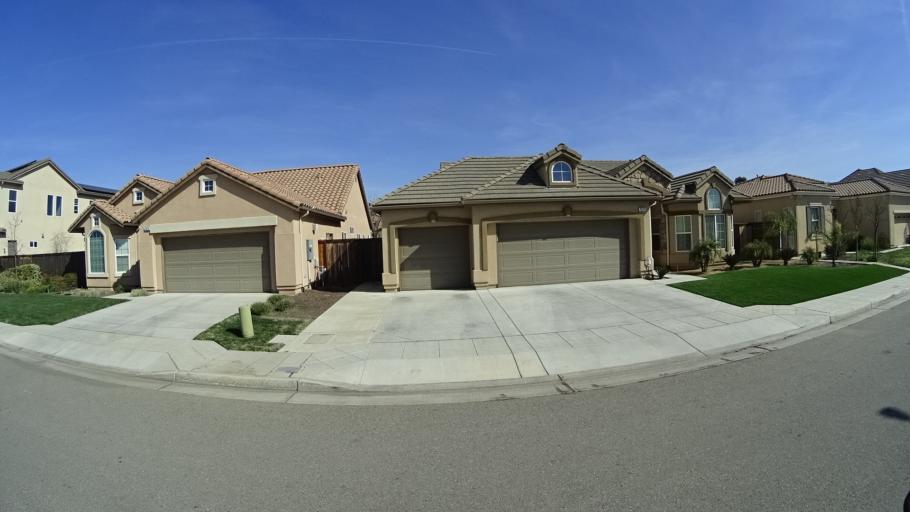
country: US
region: California
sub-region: Fresno County
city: Clovis
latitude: 36.8511
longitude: -119.7328
